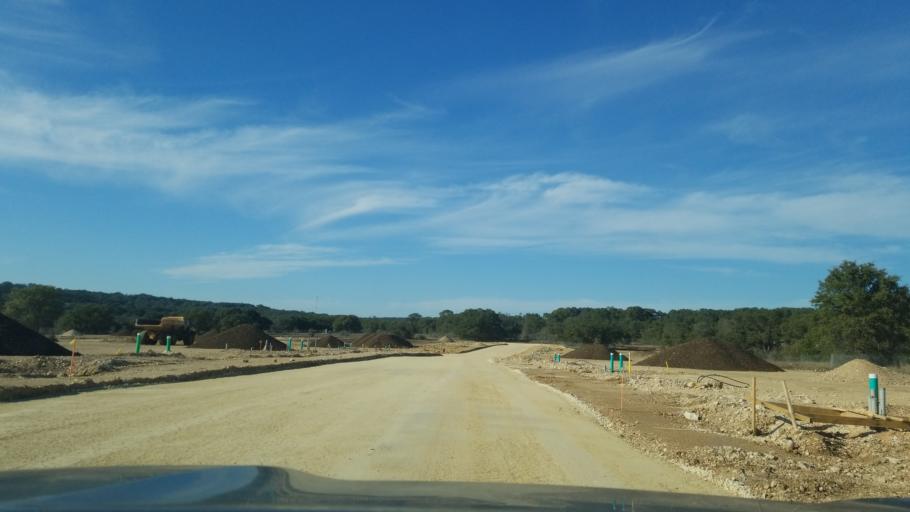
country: US
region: Texas
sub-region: Comal County
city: Canyon Lake
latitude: 29.7877
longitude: -98.2871
